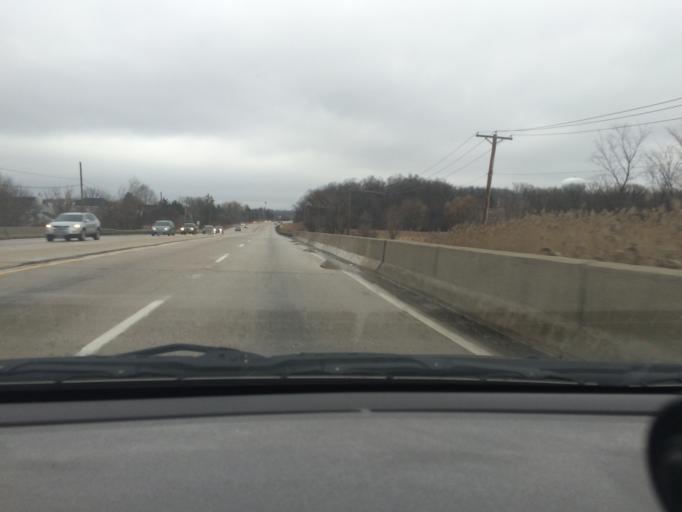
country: US
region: Illinois
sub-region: Cook County
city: Streamwood
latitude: 42.0235
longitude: -88.2029
